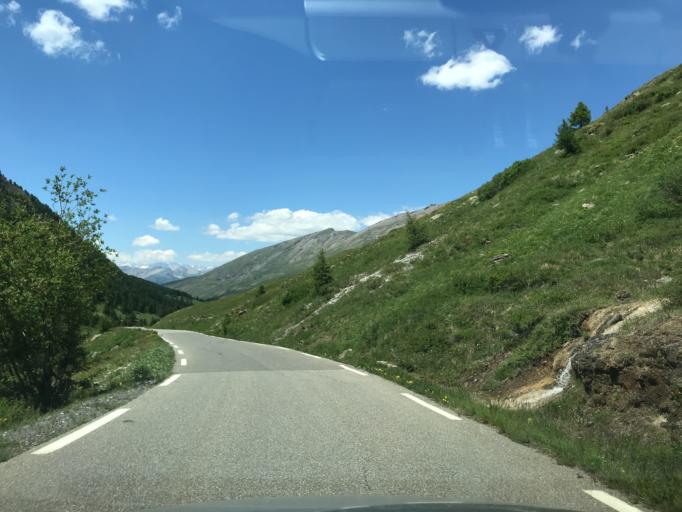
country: IT
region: Piedmont
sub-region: Provincia di Cuneo
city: Pontechianale
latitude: 44.7029
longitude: 6.9368
